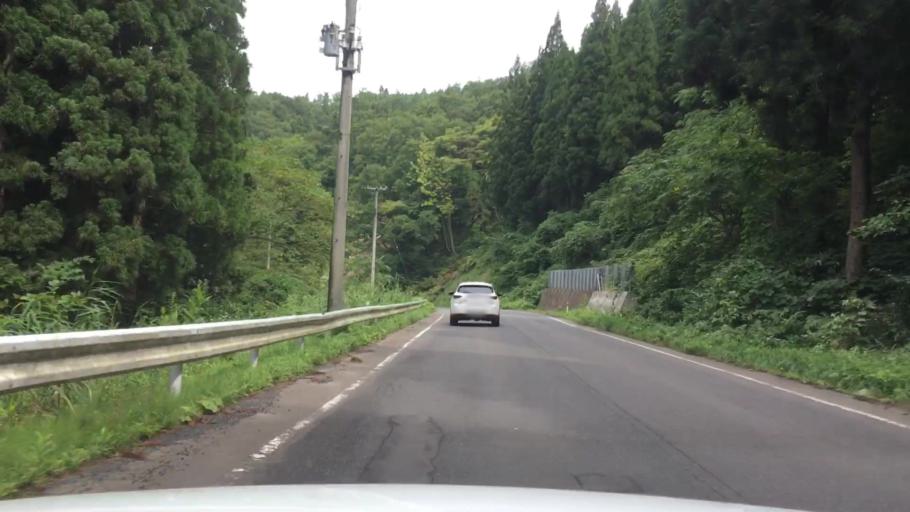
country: JP
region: Aomori
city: Shimokizukuri
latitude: 40.7345
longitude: 140.2498
